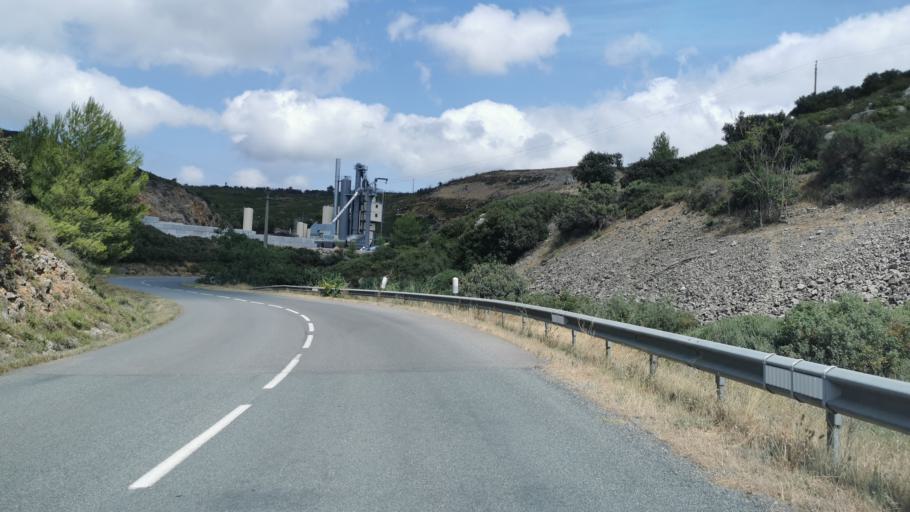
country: FR
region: Languedoc-Roussillon
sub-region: Departement de l'Aude
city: Bizanet
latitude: 43.1673
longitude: 2.9015
